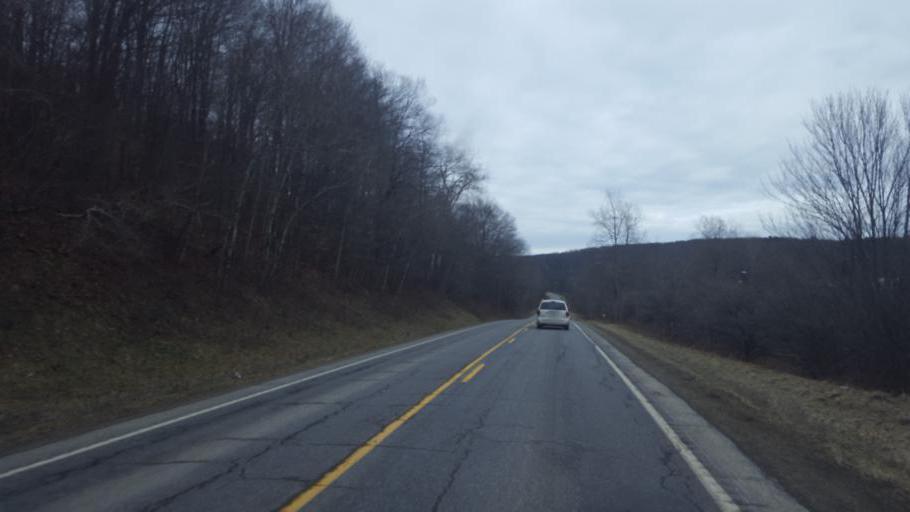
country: US
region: Pennsylvania
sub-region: Potter County
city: Coudersport
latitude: 41.8349
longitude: -77.9174
